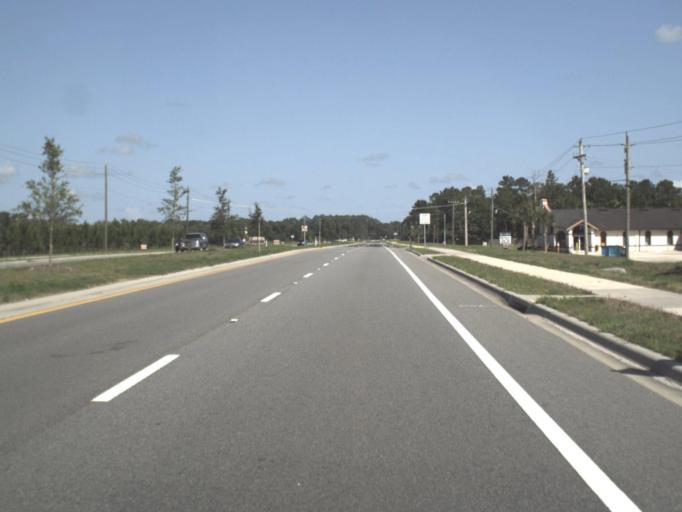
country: US
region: Florida
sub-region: Clay County
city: Green Cove Springs
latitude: 29.9741
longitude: -81.5088
